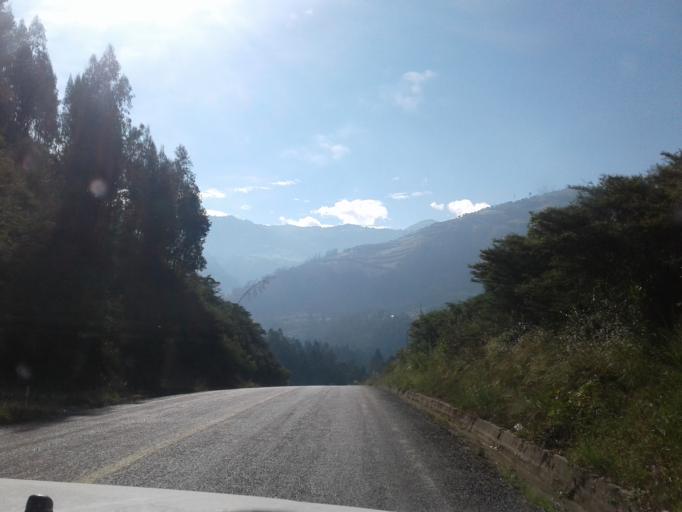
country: EC
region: Chimborazo
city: Guano
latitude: -1.5187
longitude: -78.5107
